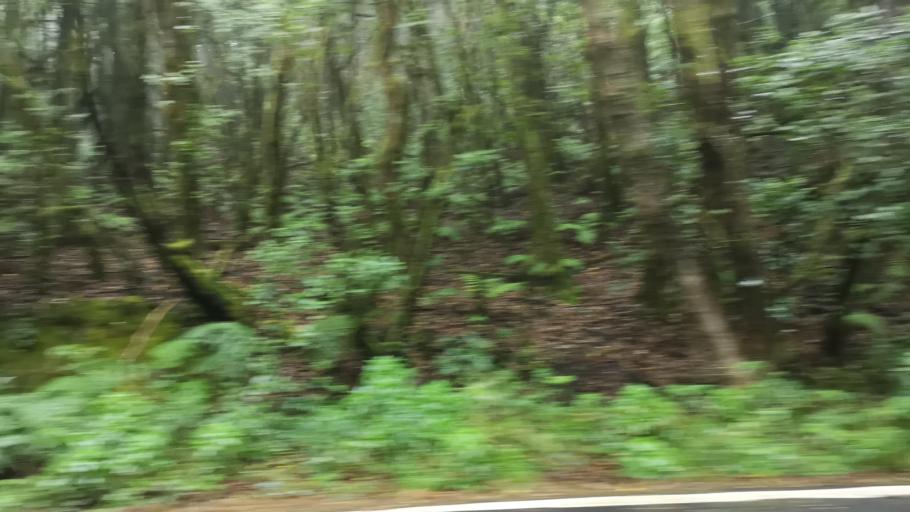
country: ES
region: Canary Islands
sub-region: Provincia de Santa Cruz de Tenerife
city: Hermigua
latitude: 28.1230
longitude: -17.2119
